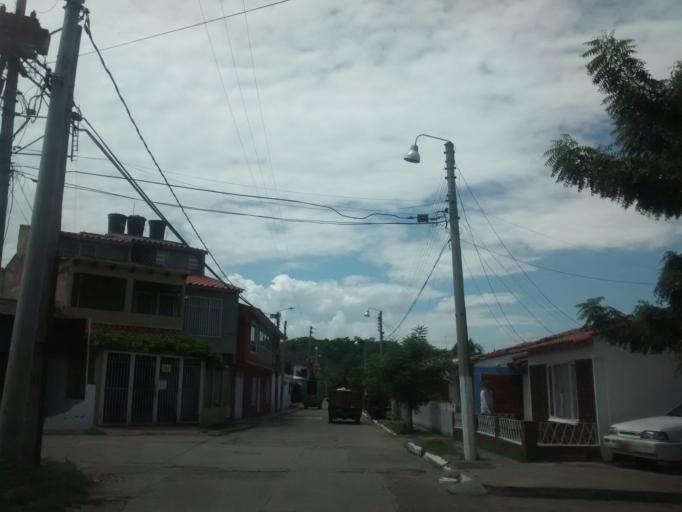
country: CO
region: Cundinamarca
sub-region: Girardot
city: Girardot City
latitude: 4.3092
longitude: -74.7913
